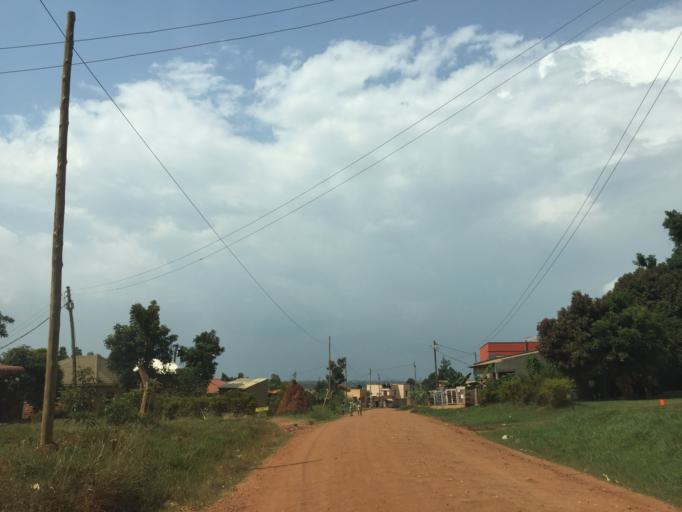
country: UG
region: Central Region
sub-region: Wakiso District
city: Kireka
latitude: 0.4119
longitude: 32.6206
